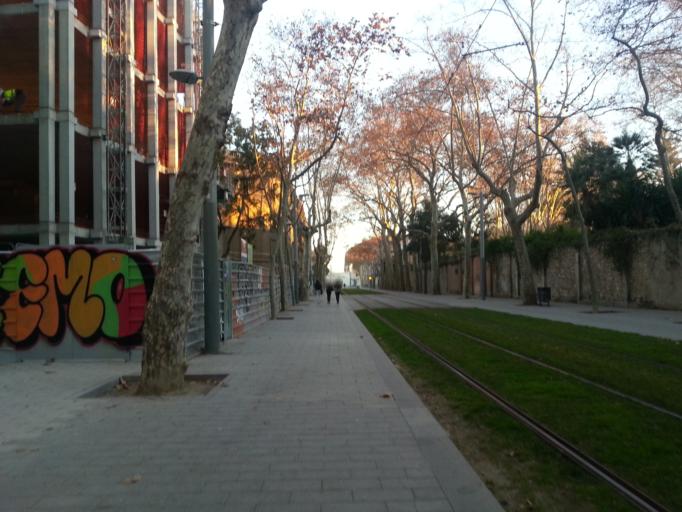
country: ES
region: Catalonia
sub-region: Provincia de Barcelona
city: Ciutat Vella
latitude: 41.3892
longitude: 2.1900
